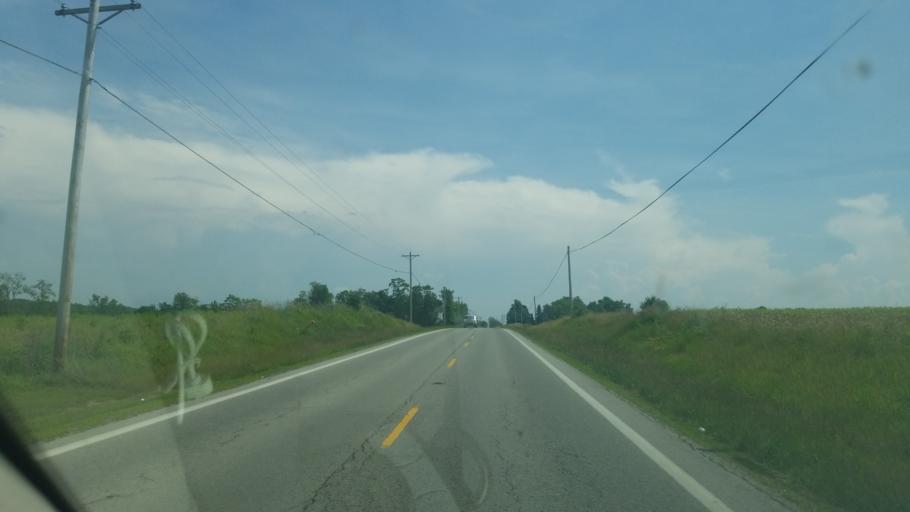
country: US
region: Ohio
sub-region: Logan County
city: Northwood
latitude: 40.4865
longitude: -83.7408
